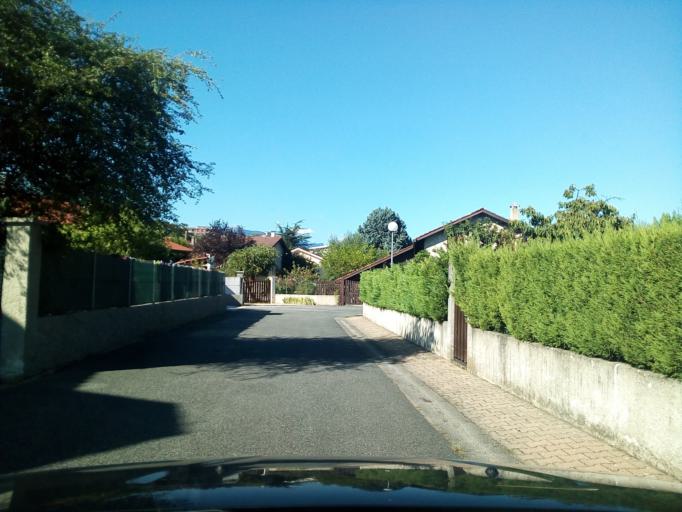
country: FR
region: Rhone-Alpes
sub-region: Departement de l'Isere
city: Echirolles
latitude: 45.1398
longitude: 5.7177
